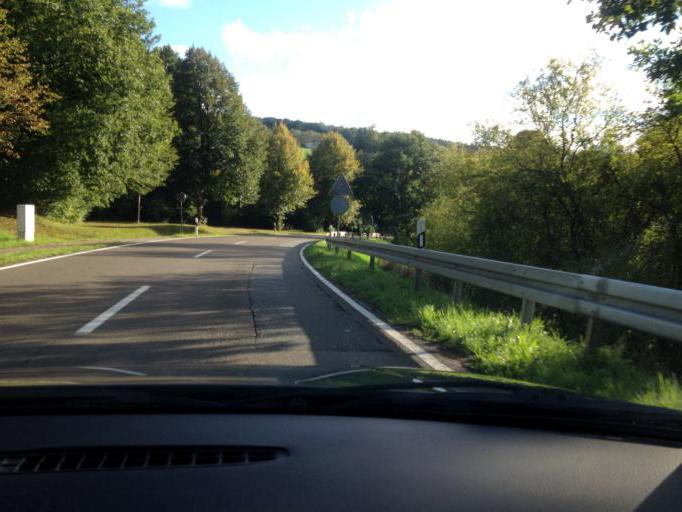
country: DE
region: Saarland
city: Marpingen
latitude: 49.4353
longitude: 7.0409
